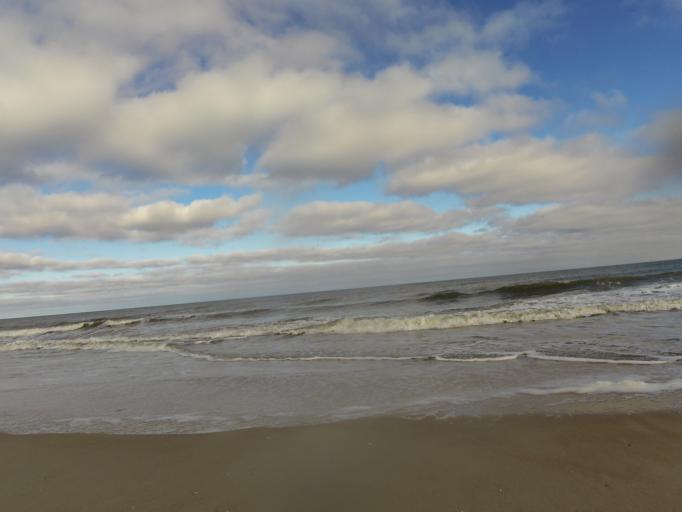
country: US
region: Florida
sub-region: Nassau County
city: Fernandina Beach
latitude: 30.5615
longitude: -81.4425
